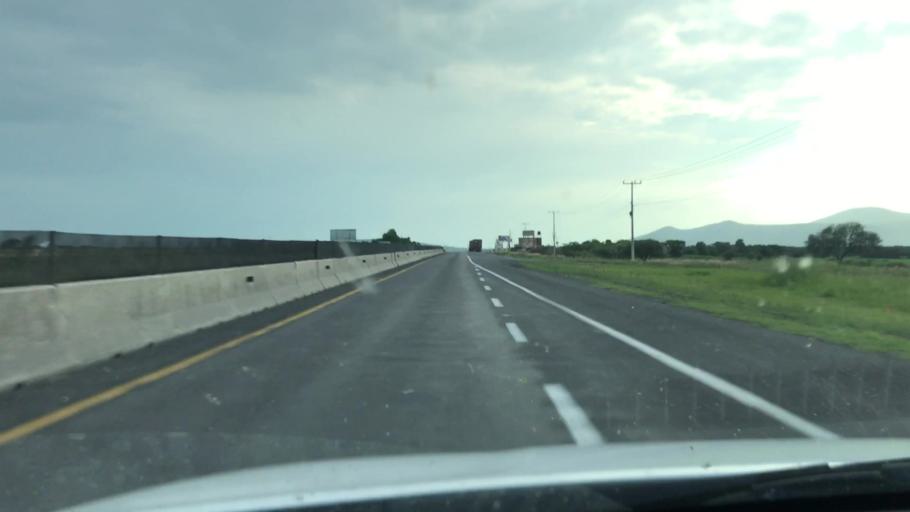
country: MX
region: Jalisco
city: Degollado
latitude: 20.3666
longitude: -102.1315
